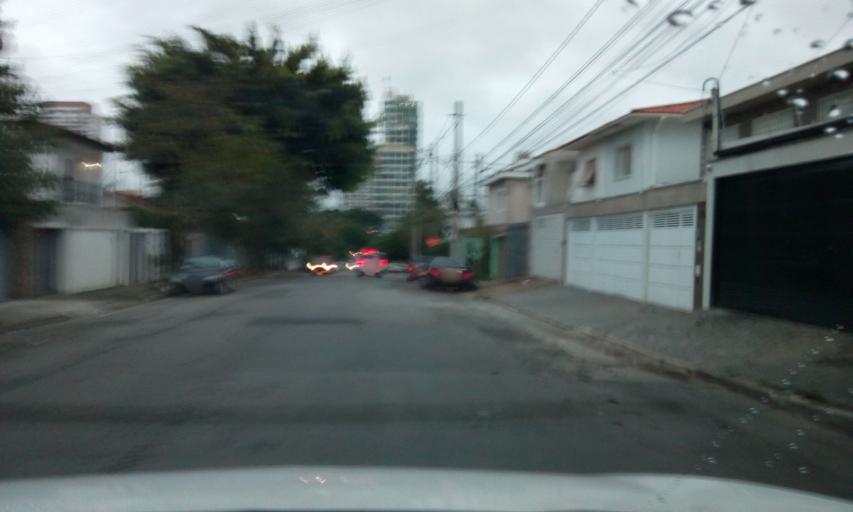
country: BR
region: Sao Paulo
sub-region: Sao Paulo
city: Sao Paulo
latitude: -23.6190
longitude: -46.6924
